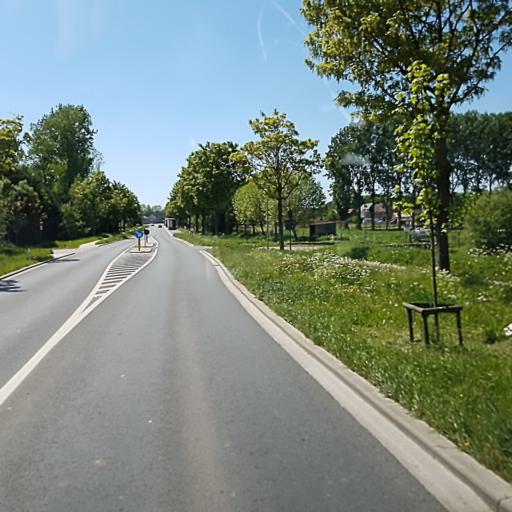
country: BE
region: Flanders
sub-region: Provincie Oost-Vlaanderen
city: Lede
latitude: 50.9369
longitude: 3.9769
